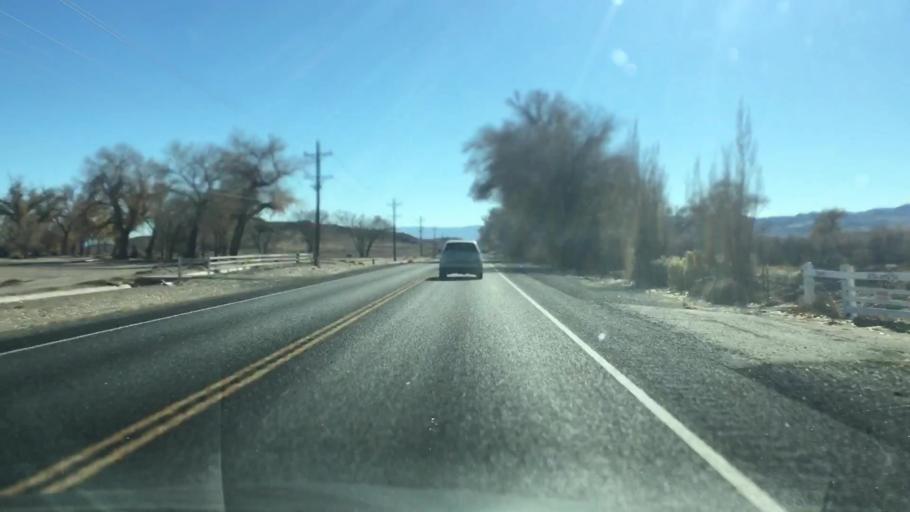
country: US
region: Nevada
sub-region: Lyon County
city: Yerington
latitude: 39.0327
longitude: -119.1816
